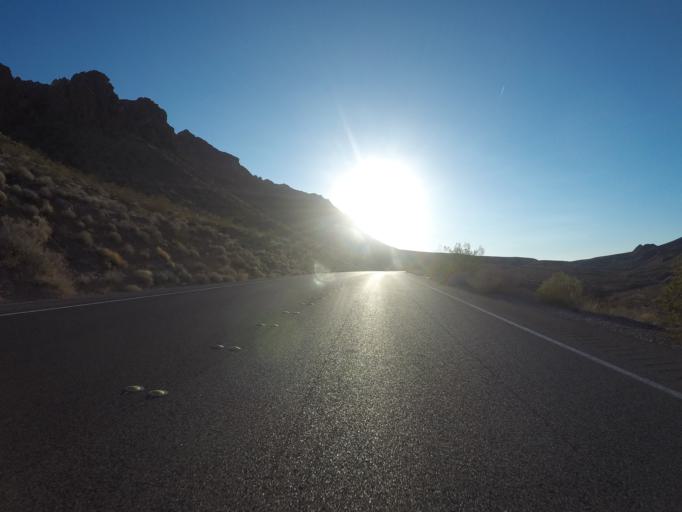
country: US
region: Nevada
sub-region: Clark County
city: Moapa Valley
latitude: 36.2458
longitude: -114.4927
